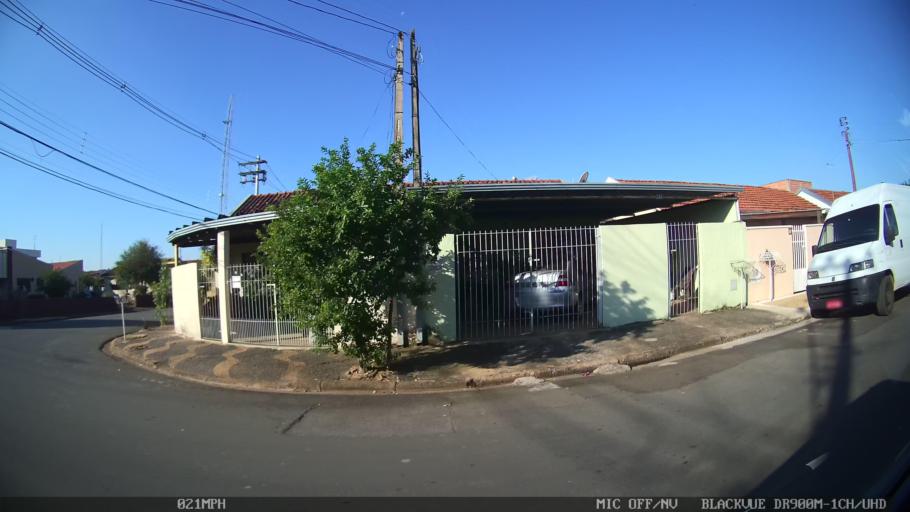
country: BR
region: Sao Paulo
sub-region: Nova Odessa
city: Nova Odessa
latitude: -22.7714
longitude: -47.2924
